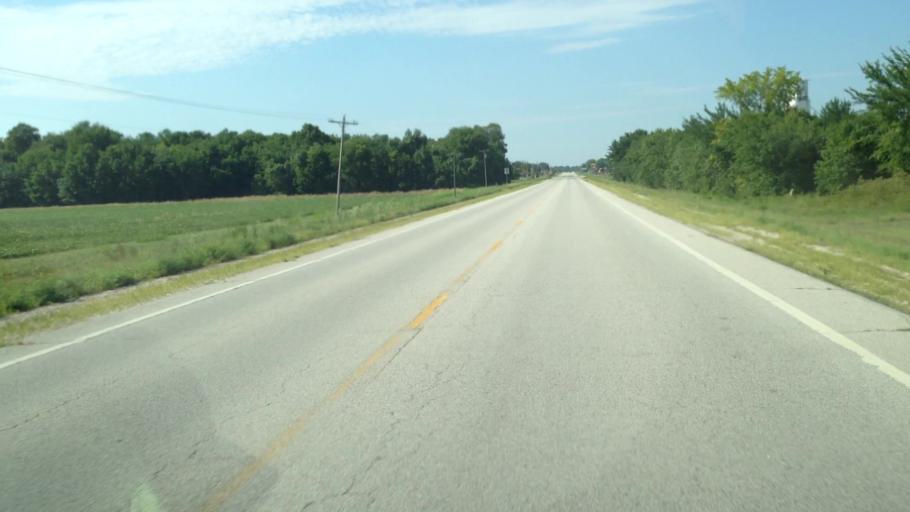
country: US
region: Kansas
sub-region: Neosho County
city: Erie
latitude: 37.5108
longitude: -95.2699
